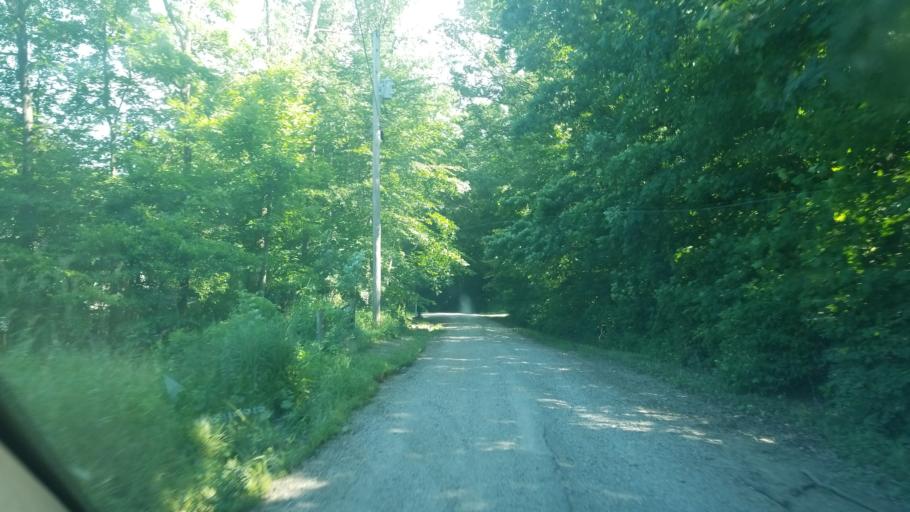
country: US
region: Ohio
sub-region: Holmes County
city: Millersburg
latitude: 40.4711
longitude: -81.9640
